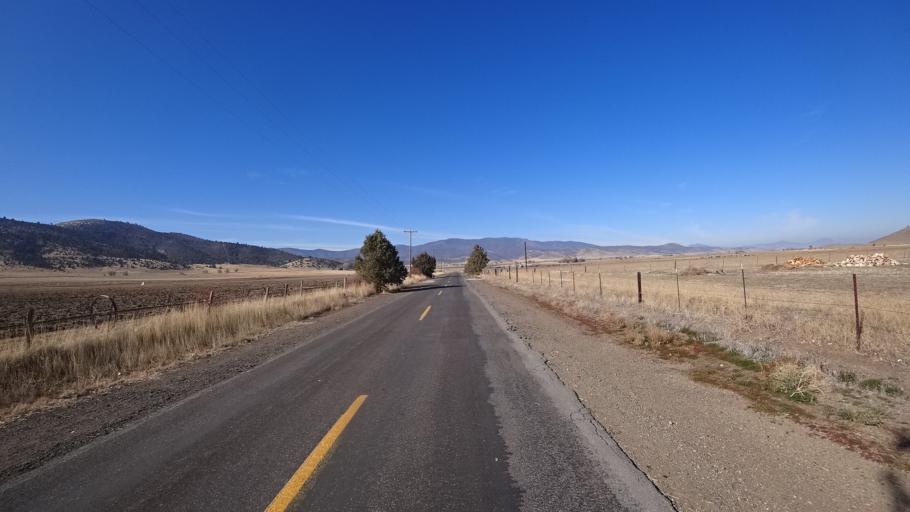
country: US
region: California
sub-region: Siskiyou County
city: Weed
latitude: 41.5217
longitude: -122.5248
